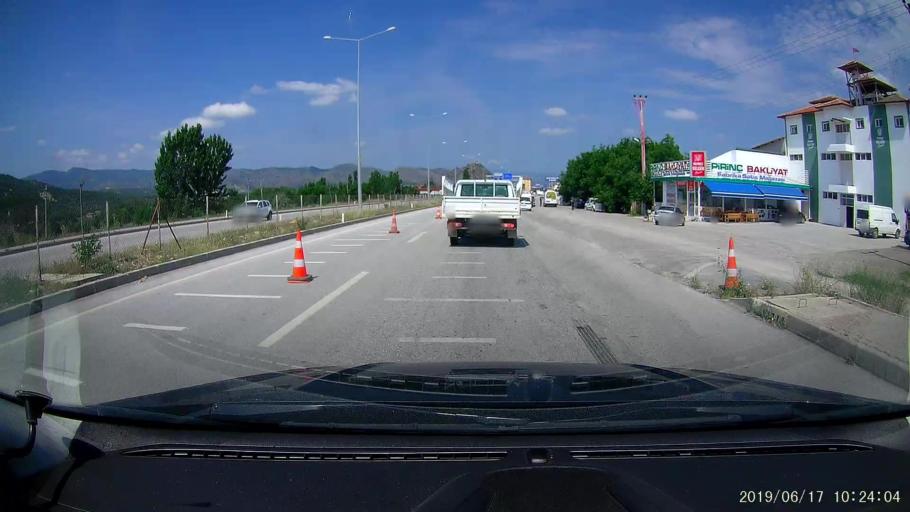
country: TR
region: Corum
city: Osmancik
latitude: 40.9707
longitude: 34.8286
